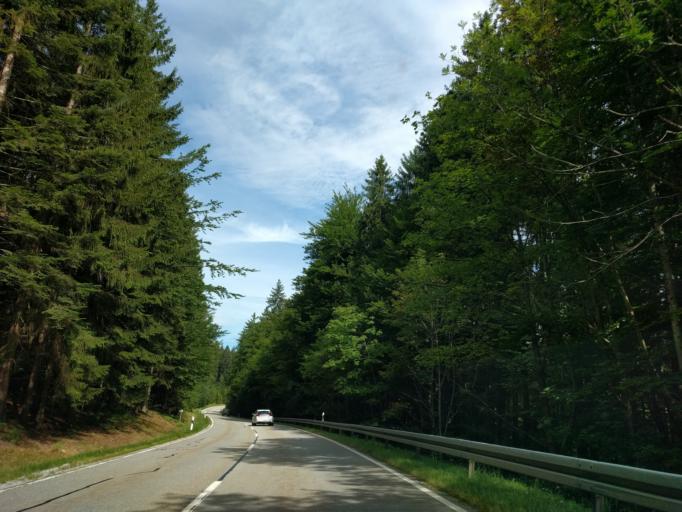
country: DE
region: Bavaria
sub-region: Lower Bavaria
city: Langdorf
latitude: 49.0353
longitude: 13.1208
